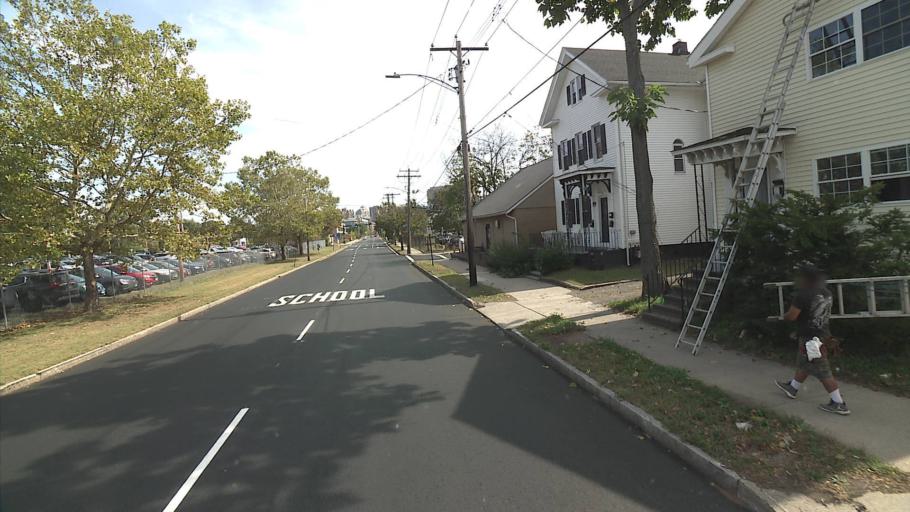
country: US
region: Connecticut
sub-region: New Haven County
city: New Haven
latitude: 41.3060
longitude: -72.9442
